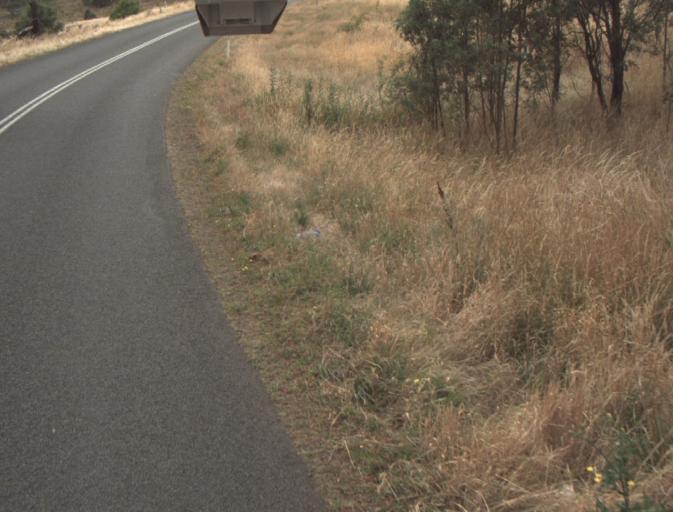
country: AU
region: Tasmania
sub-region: Northern Midlands
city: Evandale
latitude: -41.5071
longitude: 147.3659
